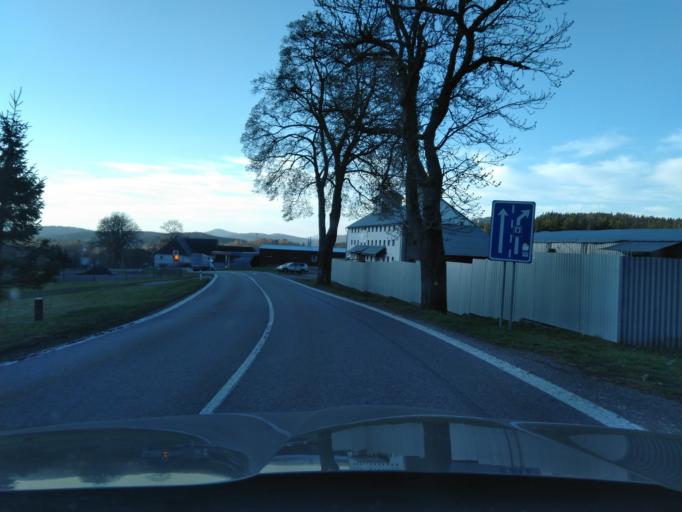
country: CZ
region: Jihocesky
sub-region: Okres Prachatice
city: Borova Lada
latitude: 48.9622
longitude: 13.7549
